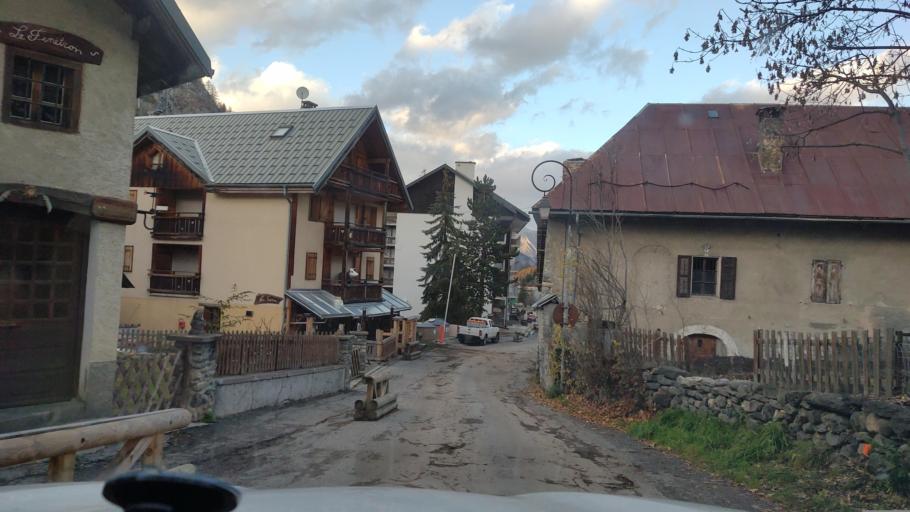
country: FR
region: Rhone-Alpes
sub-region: Departement de la Savoie
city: Valloire
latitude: 45.1632
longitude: 6.4300
